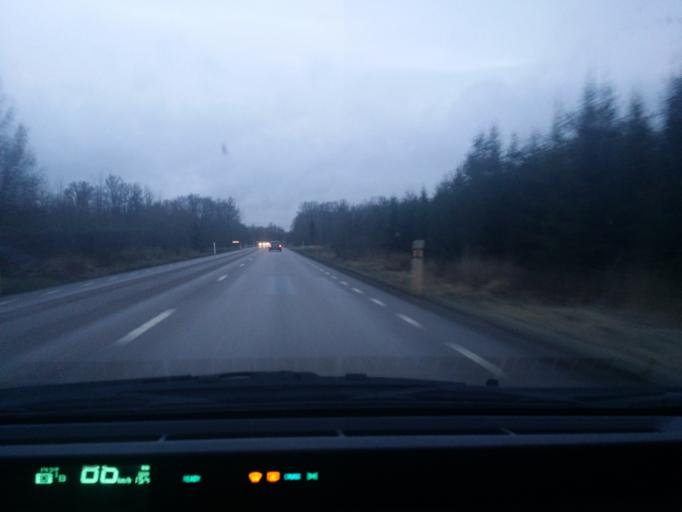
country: SE
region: Soedermanland
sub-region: Eskilstuna Kommun
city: Kvicksund
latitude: 59.4689
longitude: 16.3120
